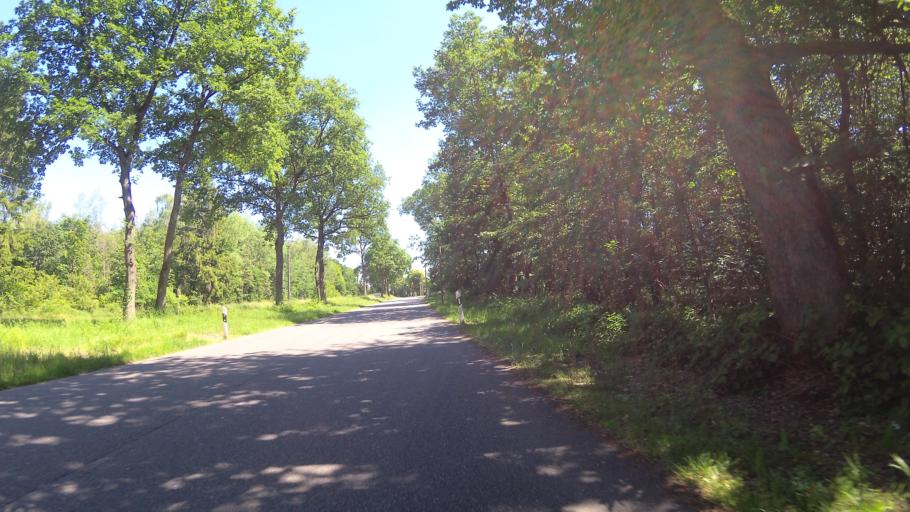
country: DE
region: Saarland
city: Saarwellingen
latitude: 49.3601
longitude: 6.7908
